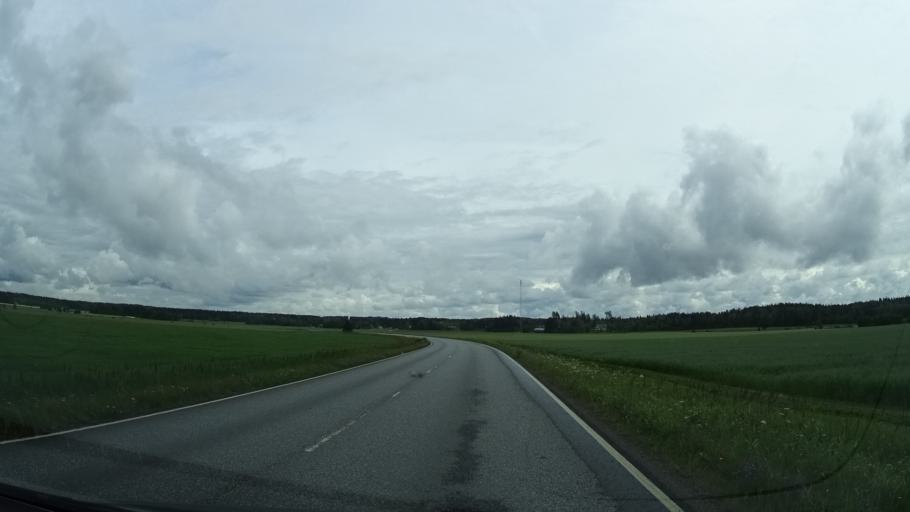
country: FI
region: Haeme
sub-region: Forssa
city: Humppila
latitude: 61.0998
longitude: 23.2955
